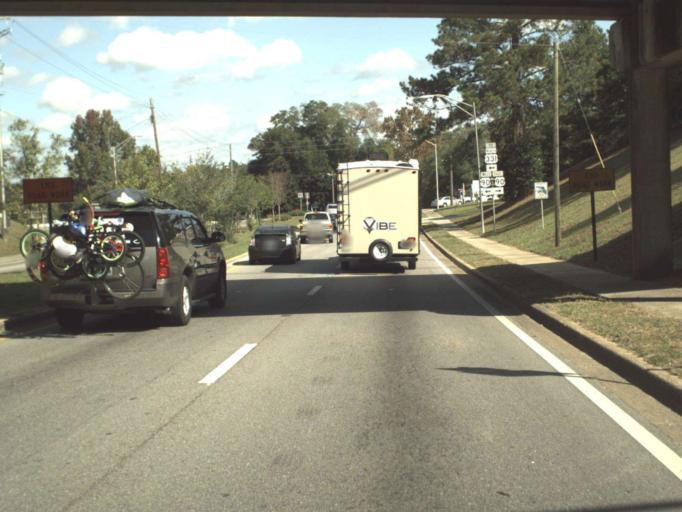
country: US
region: Florida
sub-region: Walton County
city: DeFuniak Springs
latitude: 30.7206
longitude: -86.1208
